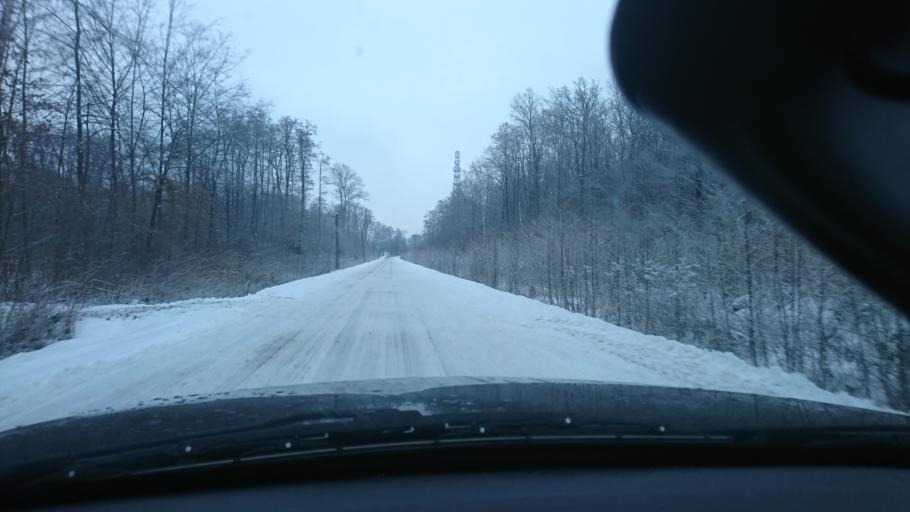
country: PL
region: Masovian Voivodeship
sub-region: Powiat ciechanowski
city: Glinojeck
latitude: 52.7497
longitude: 20.3108
